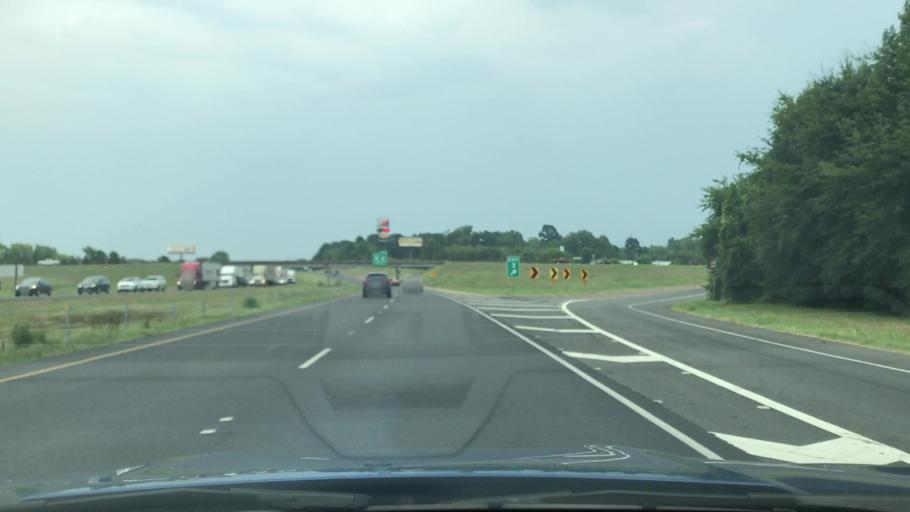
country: US
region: Louisiana
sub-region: Caddo Parish
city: Greenwood
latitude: 32.4475
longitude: -93.9833
